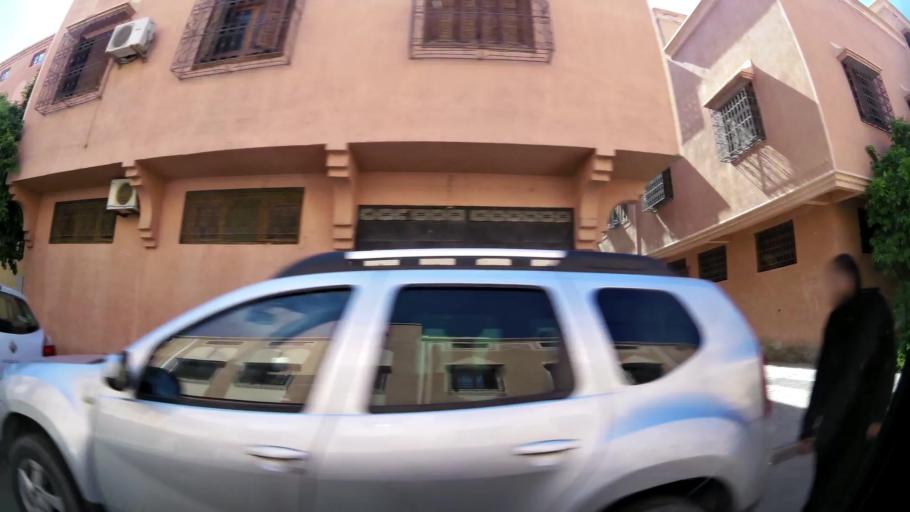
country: MA
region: Marrakech-Tensift-Al Haouz
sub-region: Marrakech
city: Marrakesh
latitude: 31.6443
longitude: -7.9790
